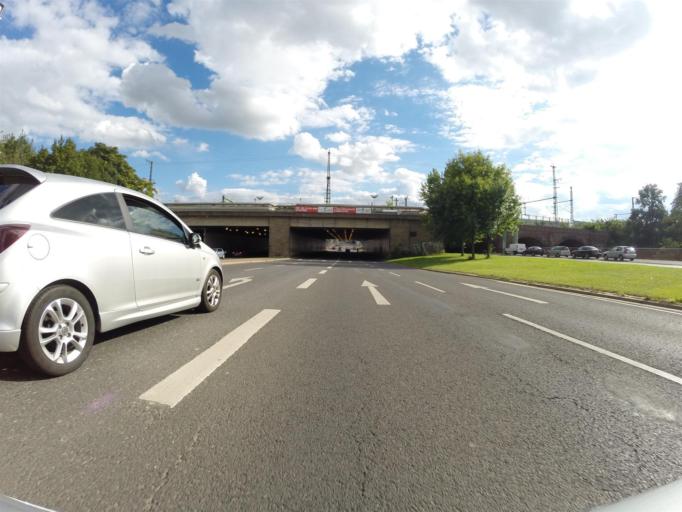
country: DE
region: Thuringia
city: Erfurt
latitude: 50.9744
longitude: 11.0422
